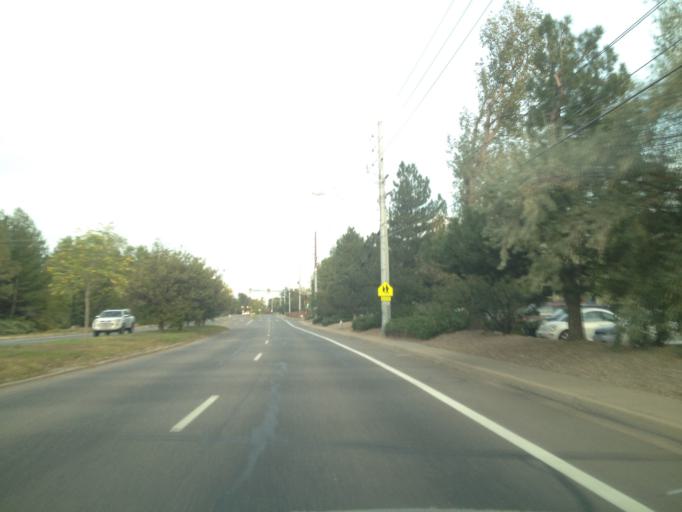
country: US
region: Colorado
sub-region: Boulder County
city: Boulder
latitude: 40.0000
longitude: -105.2313
